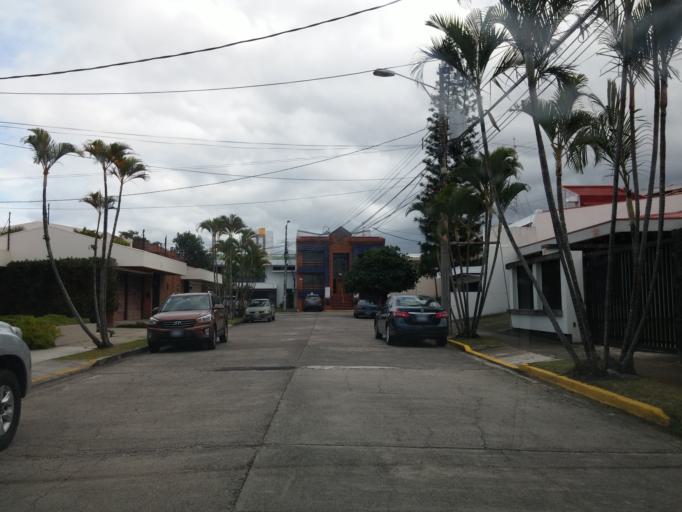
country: CR
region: San Jose
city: Colima
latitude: 9.9418
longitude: -84.1086
